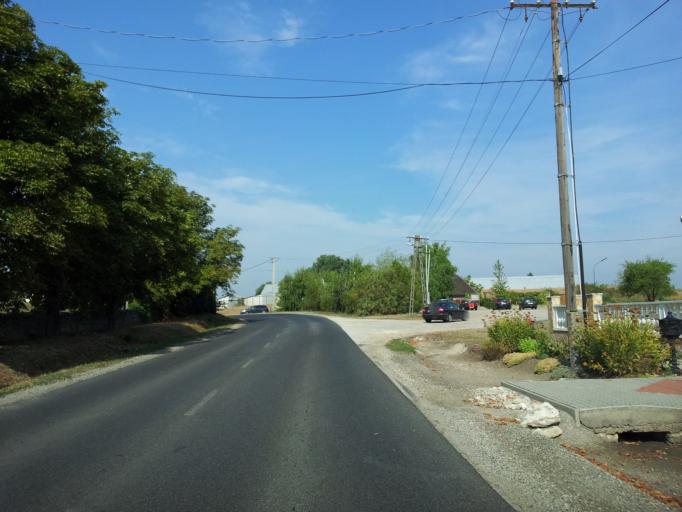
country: HU
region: Veszprem
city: Tapolca
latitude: 46.8719
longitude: 17.4756
